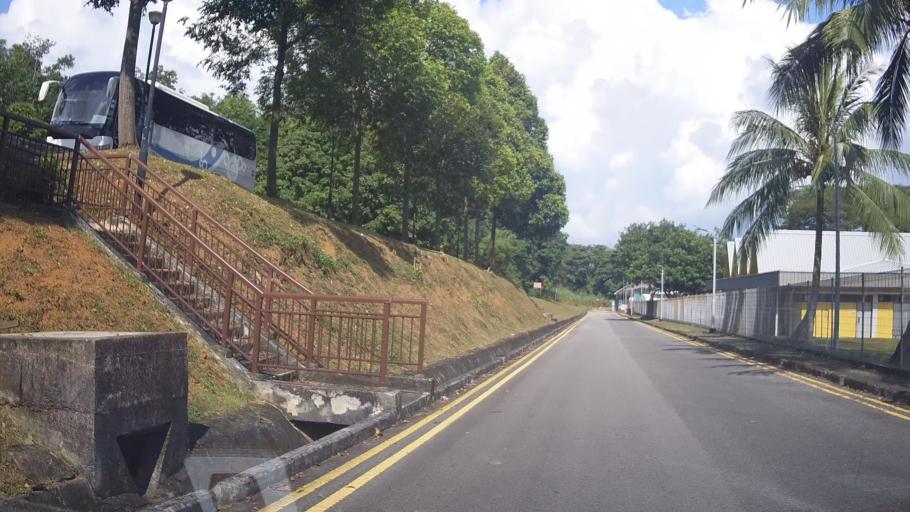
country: MY
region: Johor
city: Kampung Pasir Gudang Baru
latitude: 1.3845
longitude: 103.9430
